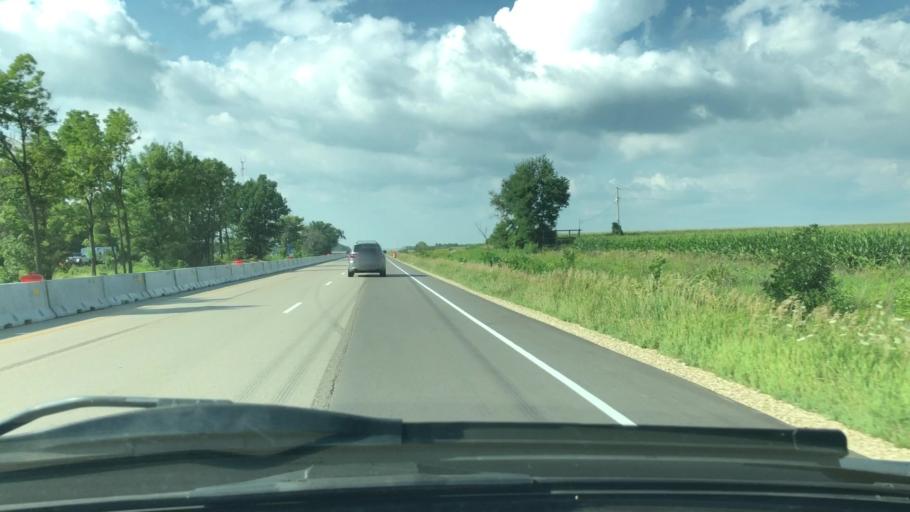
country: US
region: Wisconsin
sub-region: Rock County
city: Milton
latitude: 42.7663
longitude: -89.0045
